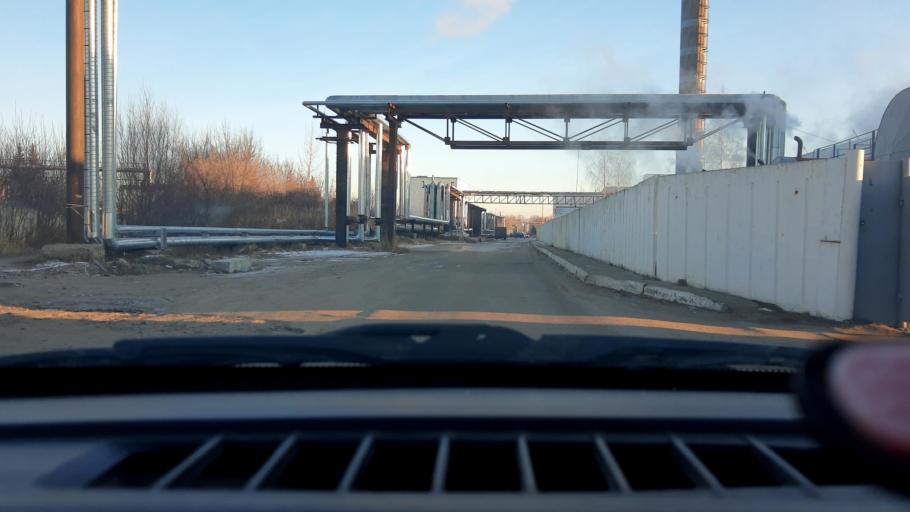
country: RU
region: Nizjnij Novgorod
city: Gorbatovka
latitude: 56.2737
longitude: 43.8346
